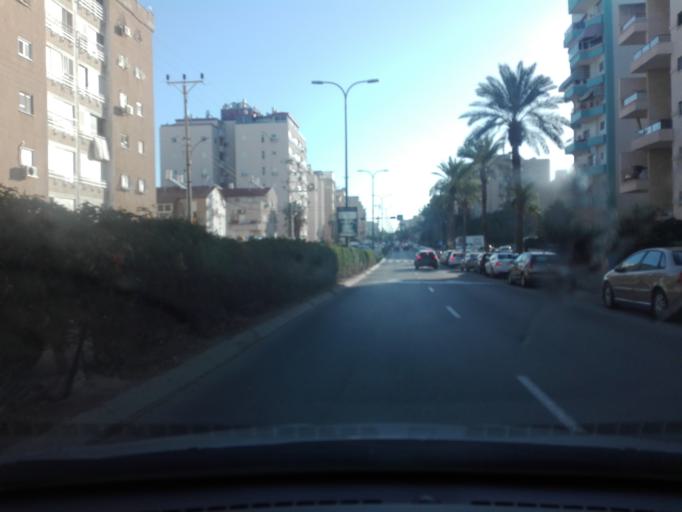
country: IL
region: Central District
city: Netanya
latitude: 32.3188
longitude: 34.8513
